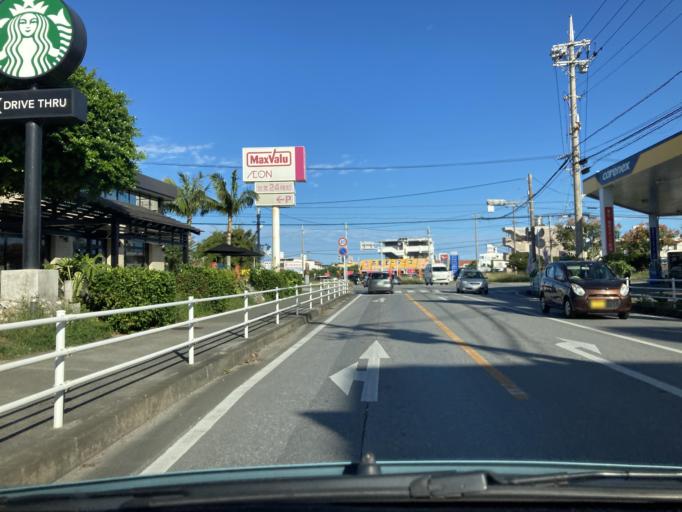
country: JP
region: Okinawa
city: Okinawa
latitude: 26.3695
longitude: 127.7468
